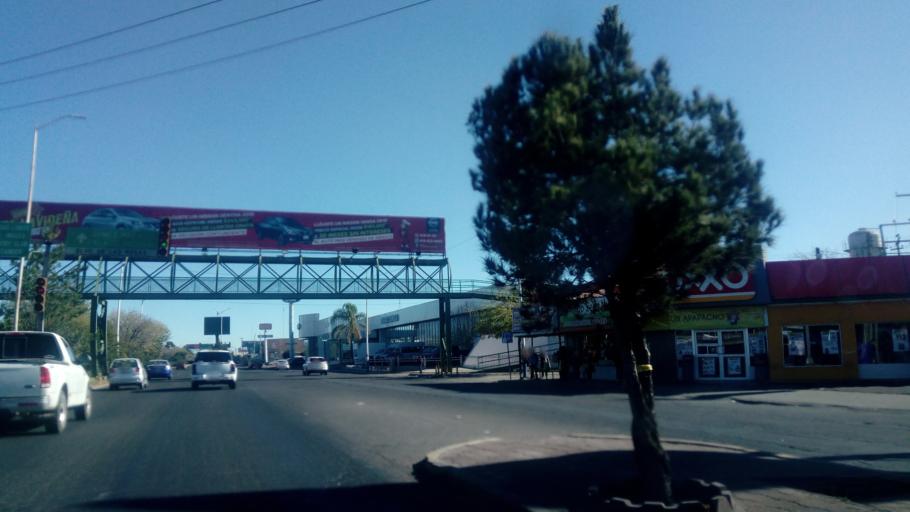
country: MX
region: Durango
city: Victoria de Durango
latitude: 24.0411
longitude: -104.6299
